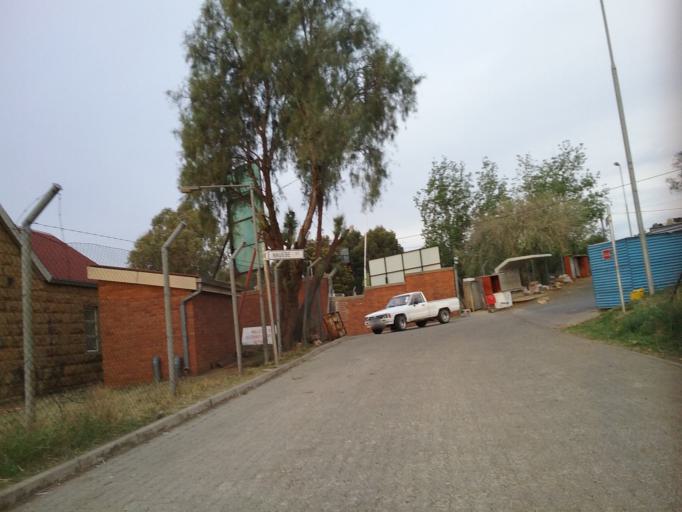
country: LS
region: Quthing
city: Quthing
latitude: -30.4061
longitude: 27.7054
